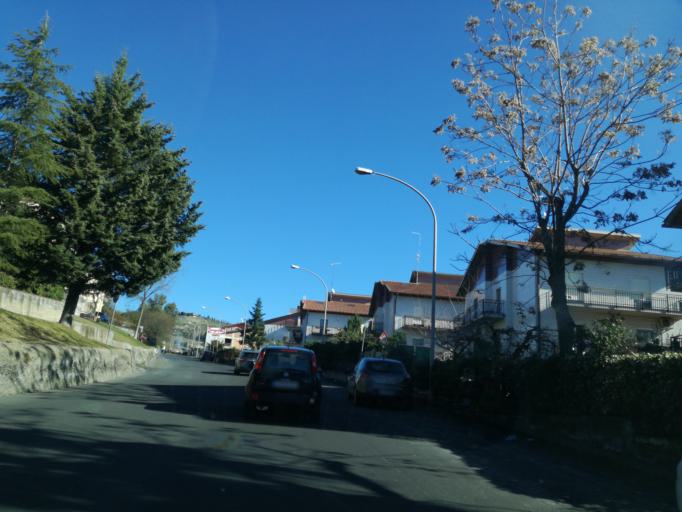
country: IT
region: Sicily
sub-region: Catania
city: Bronte
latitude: 37.7920
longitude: 14.8442
